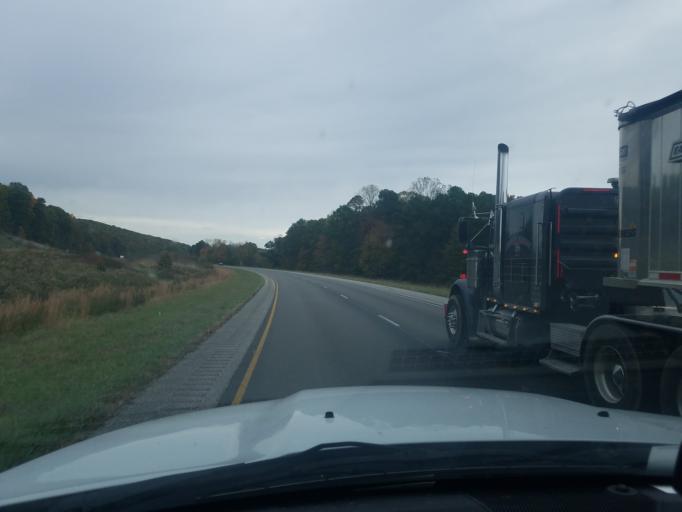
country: US
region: Indiana
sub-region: Crawford County
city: English
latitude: 38.2288
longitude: -86.5707
